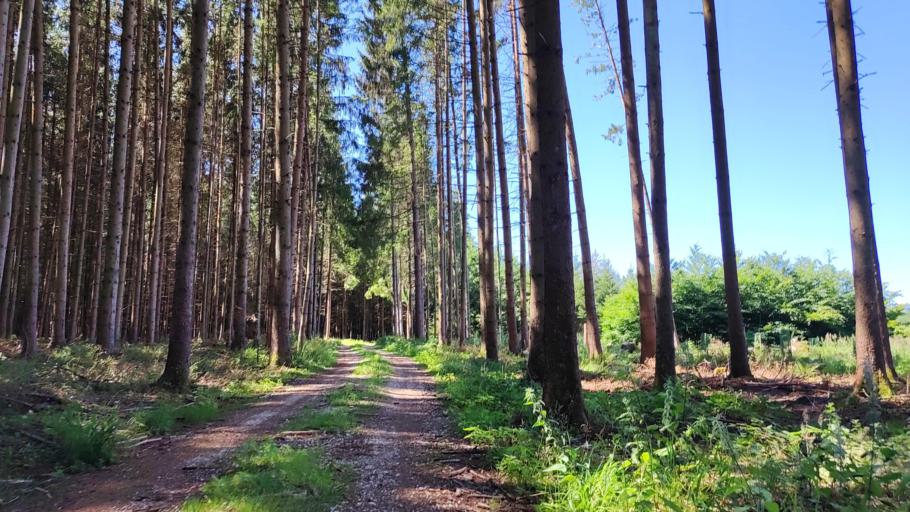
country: DE
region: Bavaria
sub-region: Swabia
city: Landensberg
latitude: 48.4599
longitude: 10.5294
